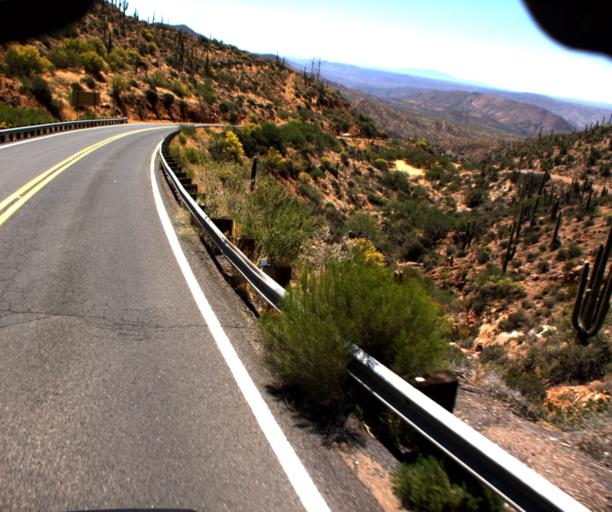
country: US
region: Arizona
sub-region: Pinal County
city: Superior
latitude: 33.1991
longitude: -111.0550
